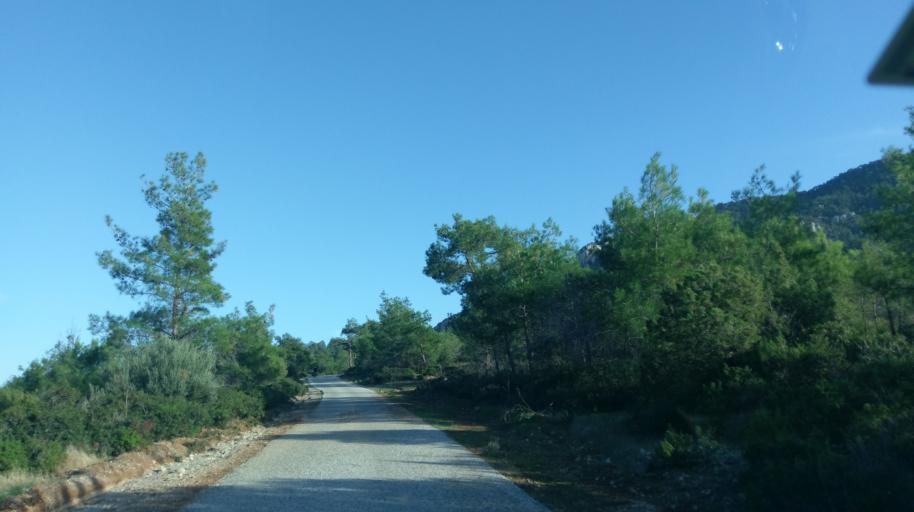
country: CY
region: Ammochostos
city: Lefkonoiko
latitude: 35.3253
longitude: 33.5905
